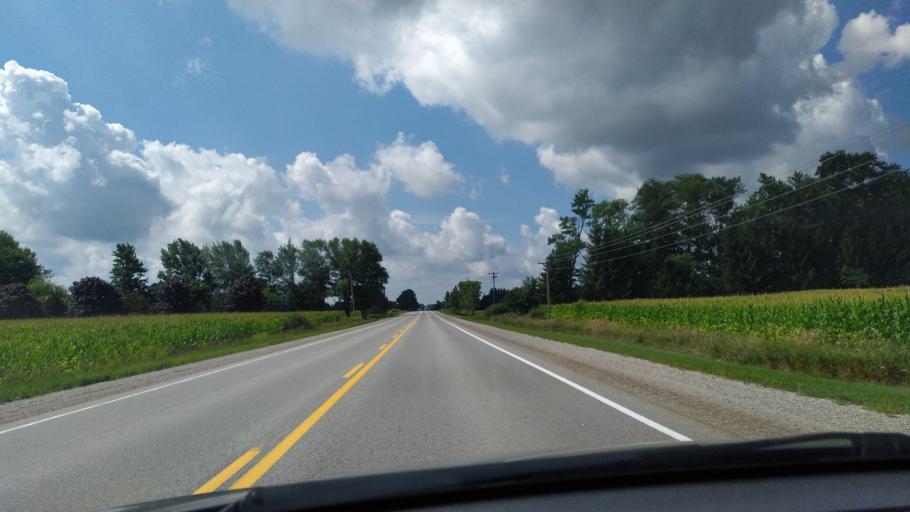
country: CA
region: Ontario
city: South Huron
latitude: 43.3511
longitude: -81.2910
